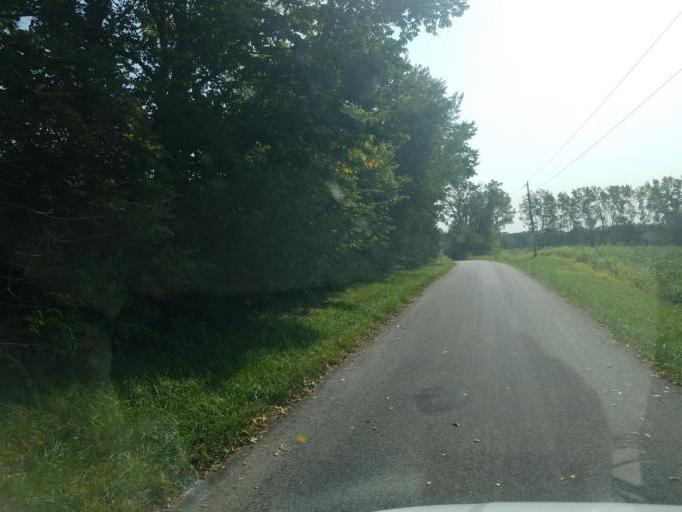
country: US
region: Ohio
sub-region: Knox County
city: Fredericktown
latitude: 40.4865
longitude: -82.6371
